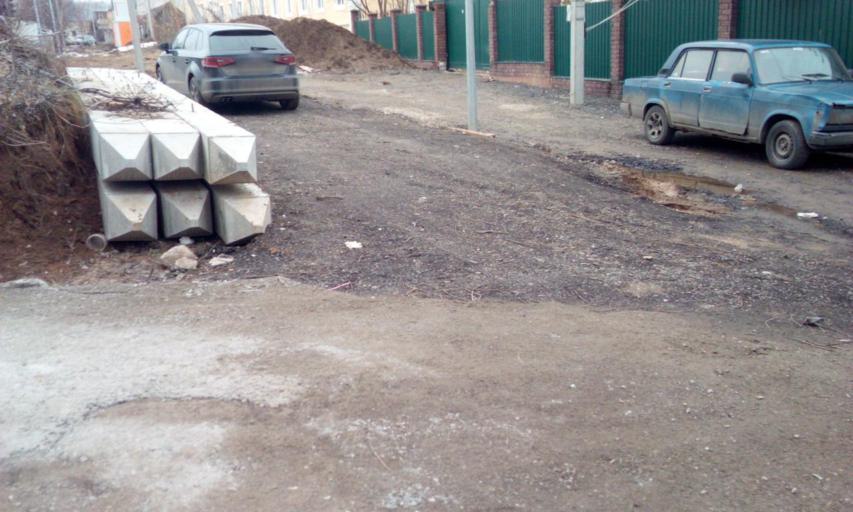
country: RU
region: Moskovskaya
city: Kommunarka
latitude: 55.5227
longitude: 37.5032
